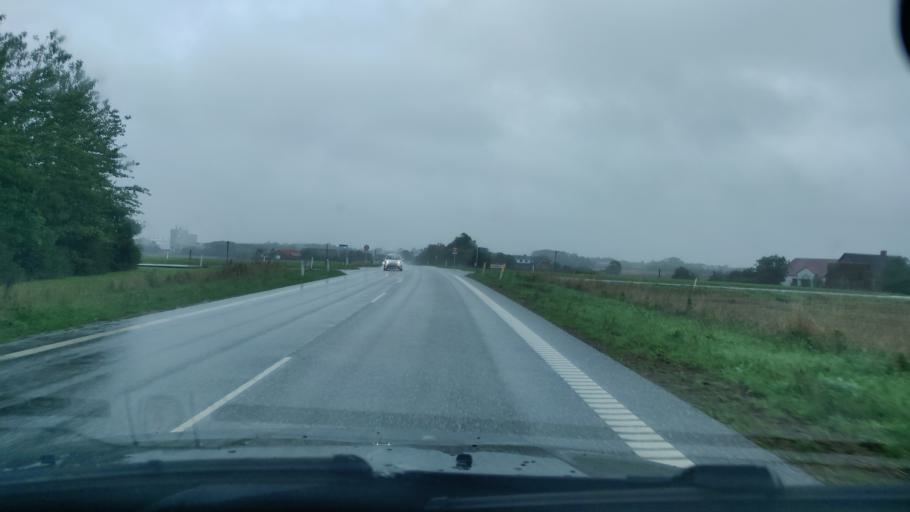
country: DK
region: North Denmark
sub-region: Thisted Kommune
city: Thisted
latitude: 56.8650
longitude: 8.5678
